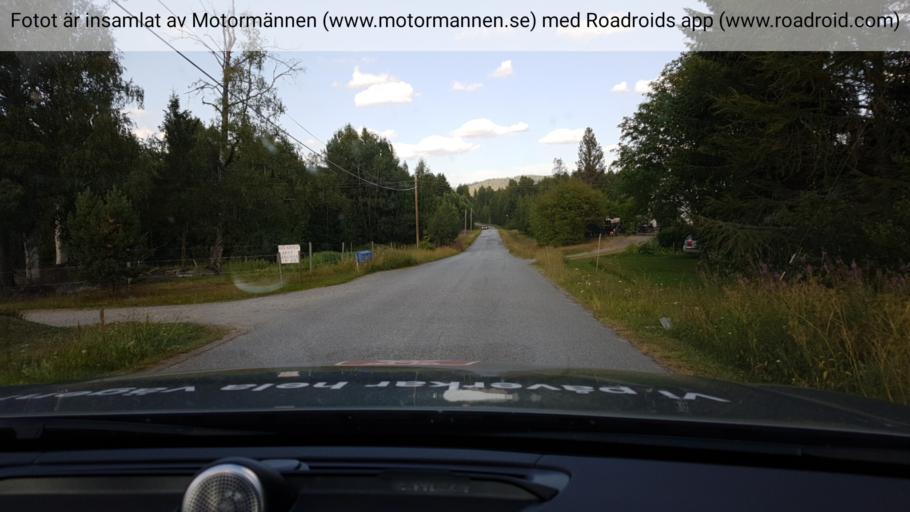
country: SE
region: Vaesterbotten
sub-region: Dorotea Kommun
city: Dorotea
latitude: 63.9174
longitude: 16.3293
